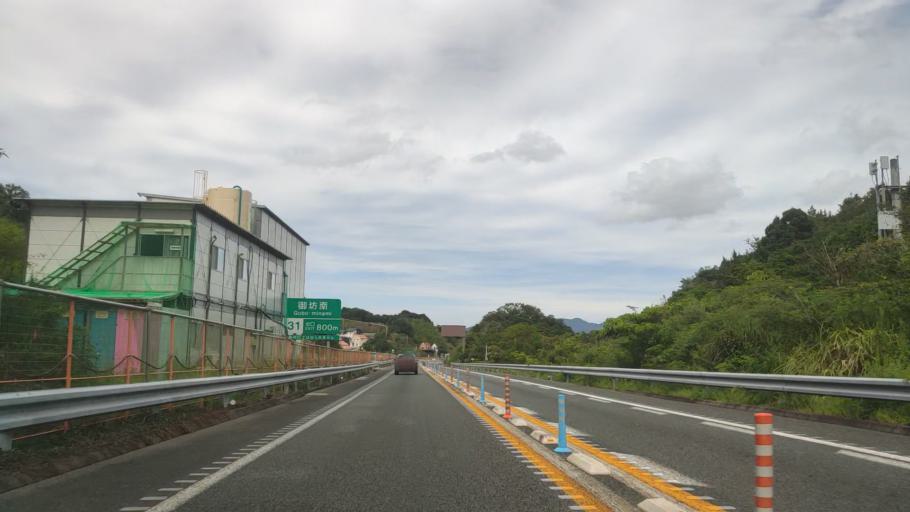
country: JP
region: Wakayama
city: Gobo
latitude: 33.8788
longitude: 135.1854
